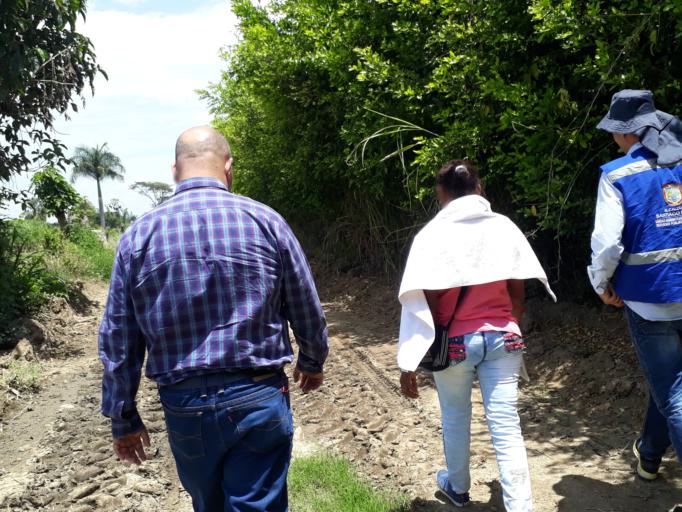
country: CO
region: Valle del Cauca
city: Cali
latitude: 3.3669
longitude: -76.4746
